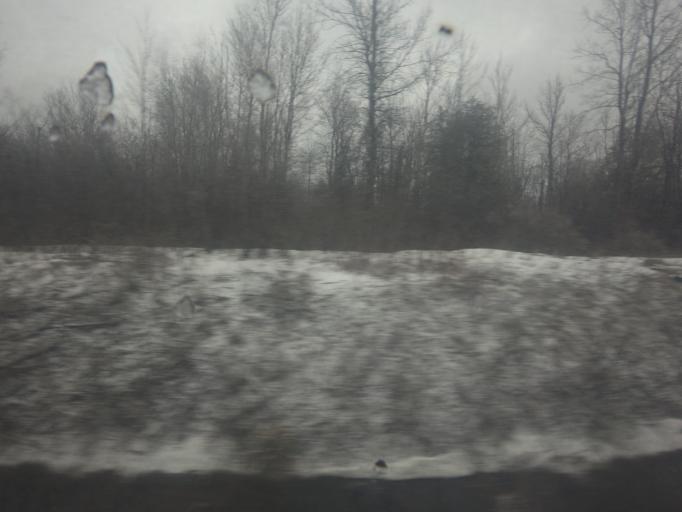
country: CA
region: Ontario
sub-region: Lanark County
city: Smiths Falls
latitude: 44.9380
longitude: -76.0243
